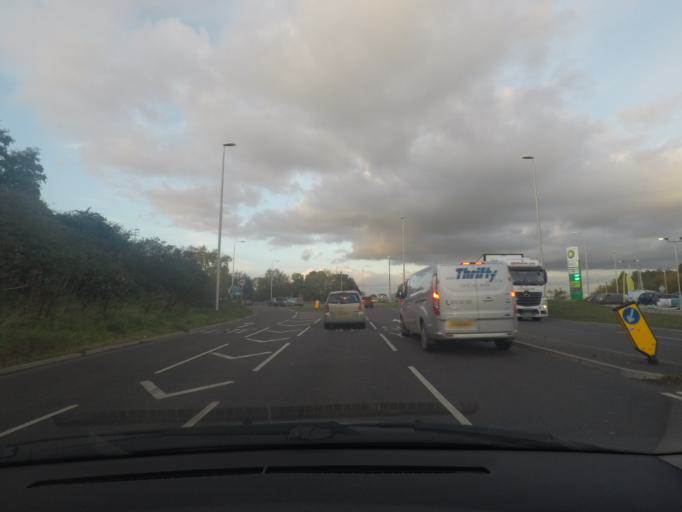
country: GB
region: England
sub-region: City of York
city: Nether Poppleton
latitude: 53.9720
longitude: -1.1439
